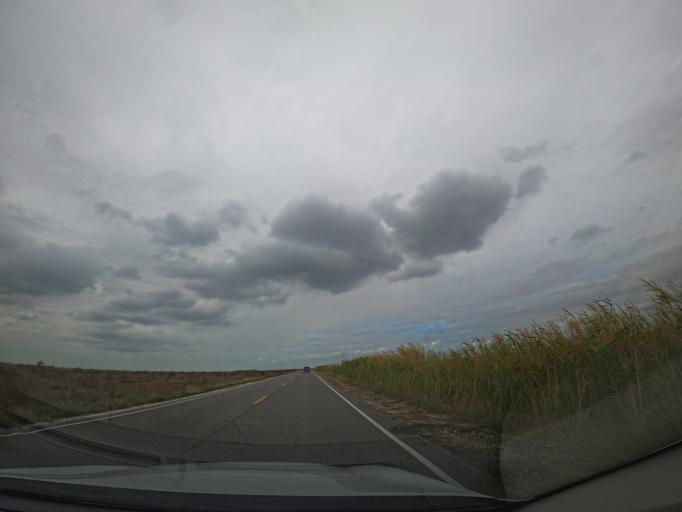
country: US
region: Louisiana
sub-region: Cameron Parish
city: Cameron
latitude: 29.7666
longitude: -93.3769
